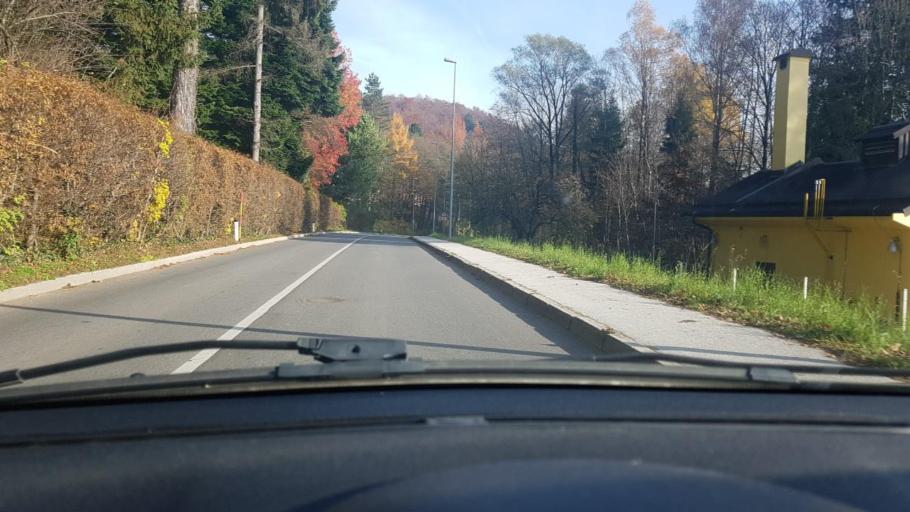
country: SI
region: Kranj
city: Golnik
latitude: 46.3271
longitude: 14.3317
